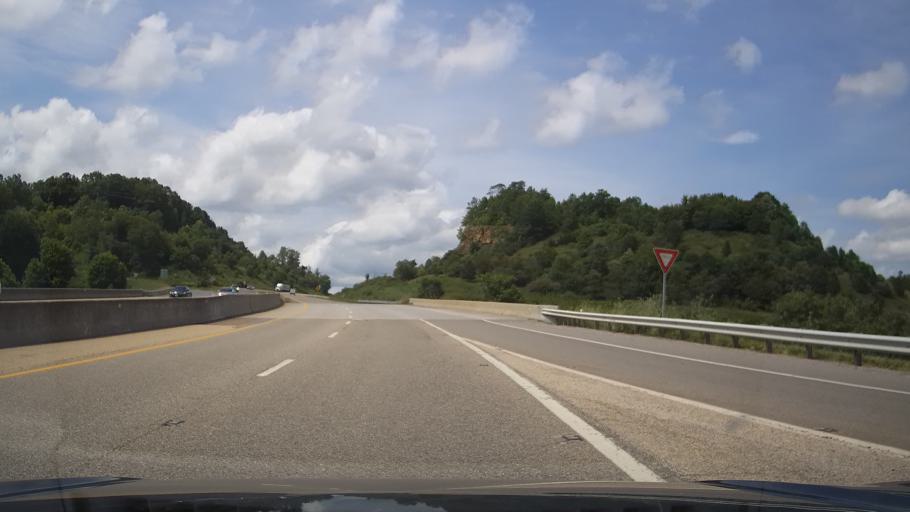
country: US
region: Virginia
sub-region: City of Norton
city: Norton
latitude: 36.9381
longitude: -82.6132
